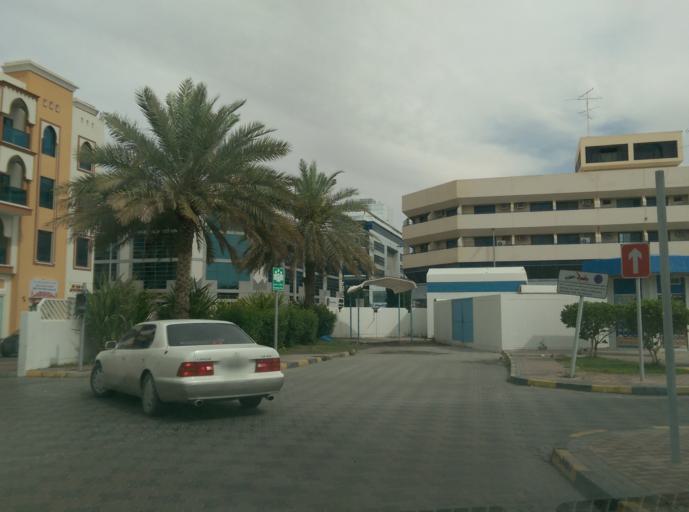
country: AE
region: Ash Shariqah
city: Sharjah
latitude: 25.2450
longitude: 55.3099
